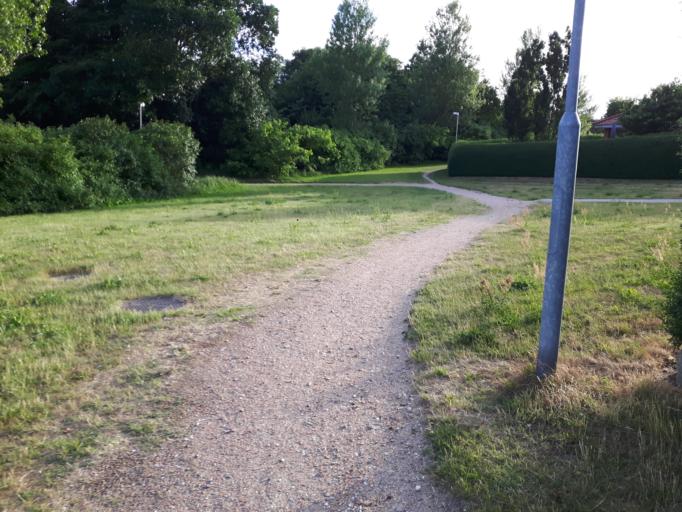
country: DK
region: Central Jutland
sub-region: Skive Kommune
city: Skive
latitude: 56.5524
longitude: 9.0531
